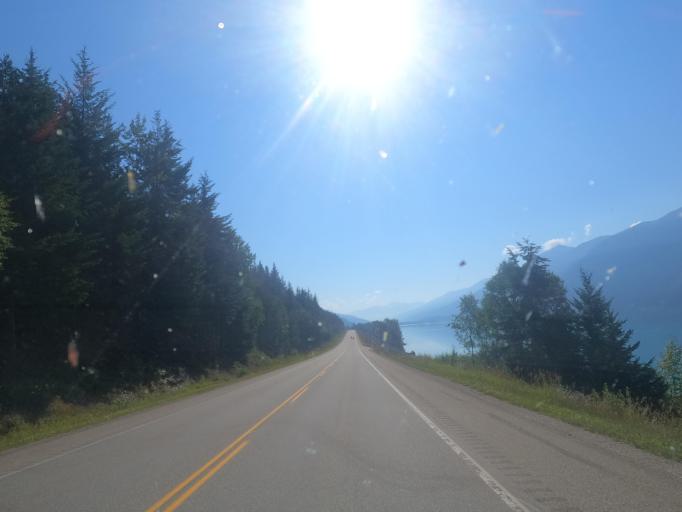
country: CA
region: Alberta
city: Jasper Park Lodge
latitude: 52.9607
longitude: -118.9068
